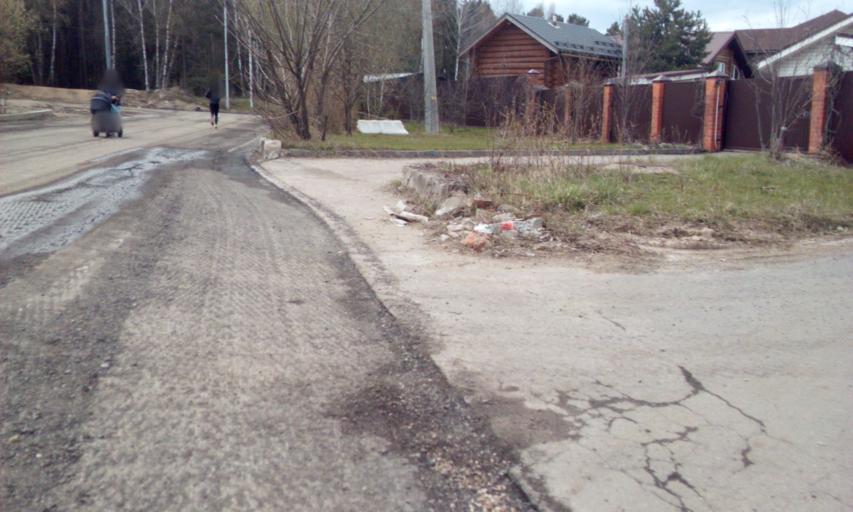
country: RU
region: Moskovskaya
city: Annino
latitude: 55.6211
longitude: 37.2570
